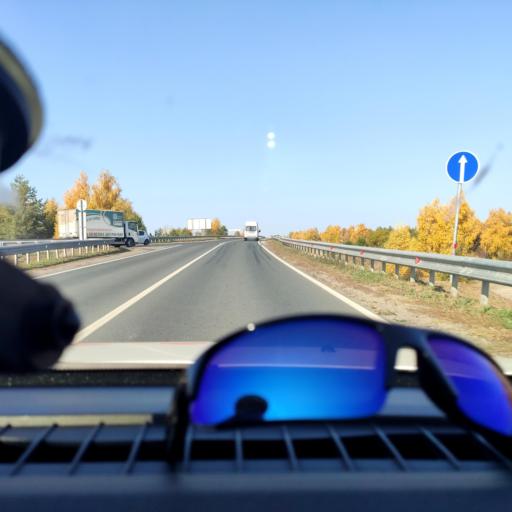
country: RU
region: Samara
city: Bereza
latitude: 53.4864
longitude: 50.1166
